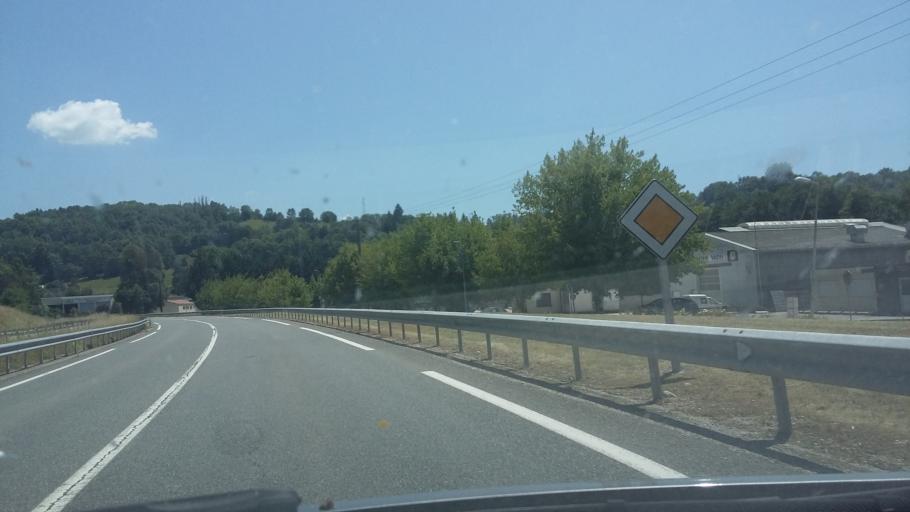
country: FR
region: Rhone-Alpes
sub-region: Departement de l'Ain
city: Belley
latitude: 45.7775
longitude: 5.6905
